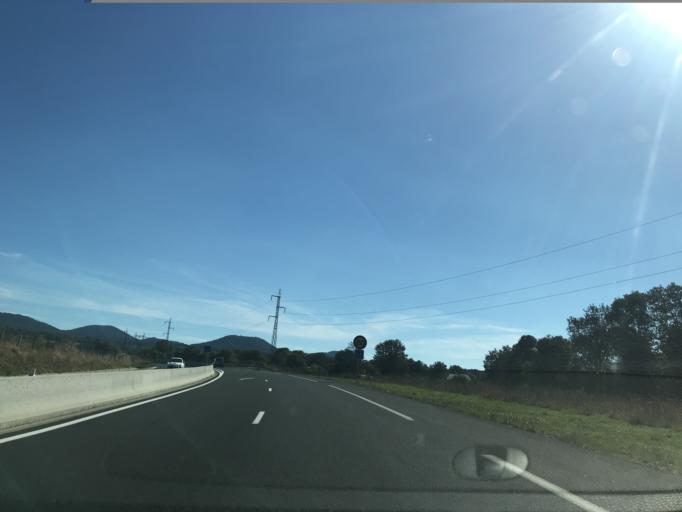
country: FR
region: Auvergne
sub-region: Departement du Puy-de-Dome
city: Gelles
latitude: 45.7329
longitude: 2.8703
